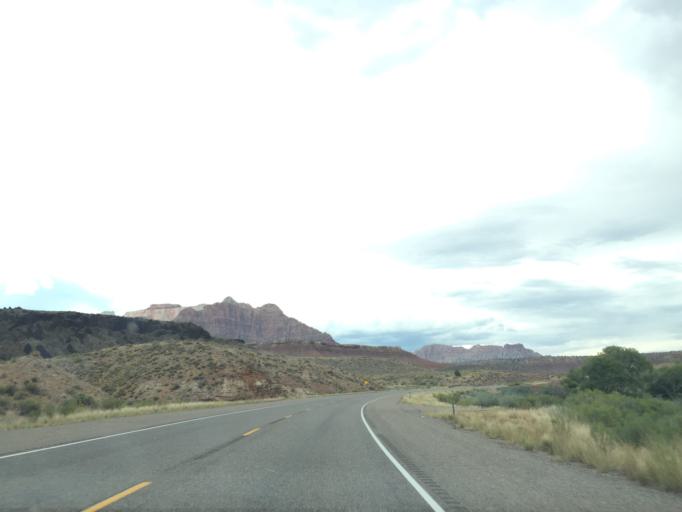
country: US
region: Utah
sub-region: Washington County
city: LaVerkin
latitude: 37.1715
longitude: -113.0922
